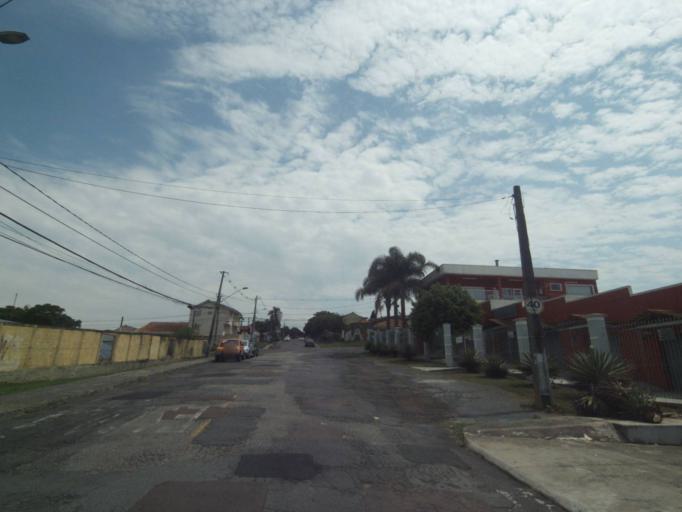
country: BR
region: Parana
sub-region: Pinhais
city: Pinhais
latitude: -25.4038
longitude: -49.2065
